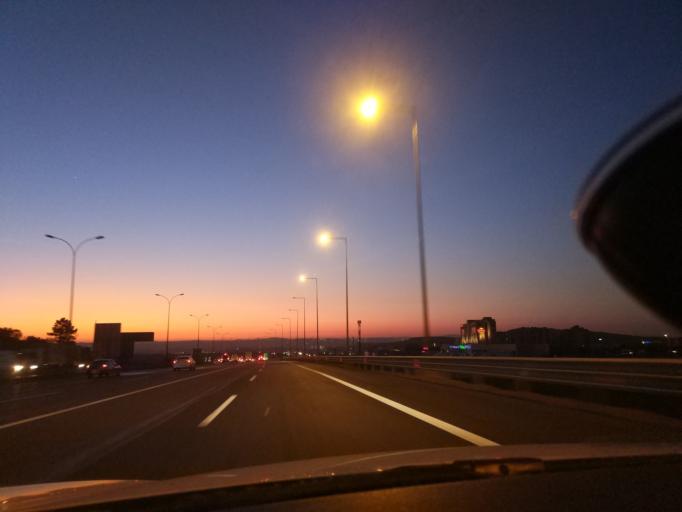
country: TR
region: Istanbul
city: Sultanbeyli
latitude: 40.9426
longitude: 29.3181
